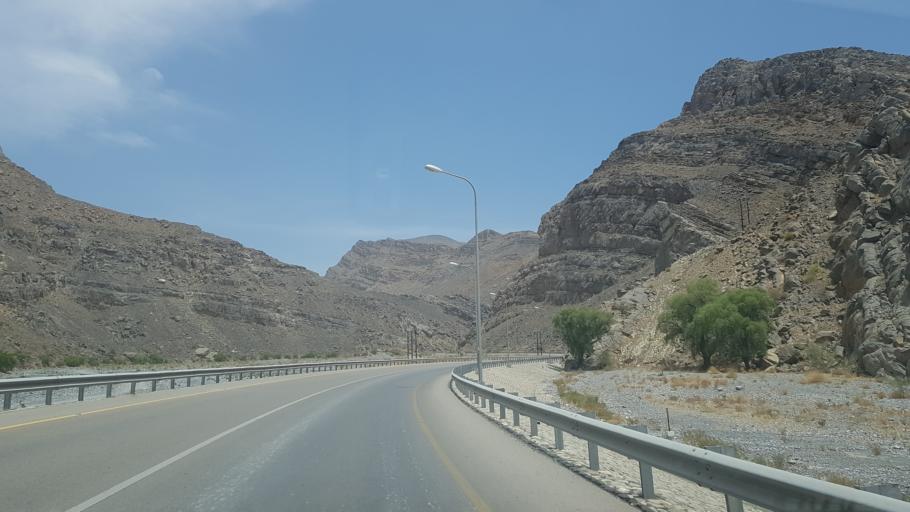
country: OM
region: Muhafazat ad Dakhiliyah
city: Izki
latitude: 22.9289
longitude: 57.6658
